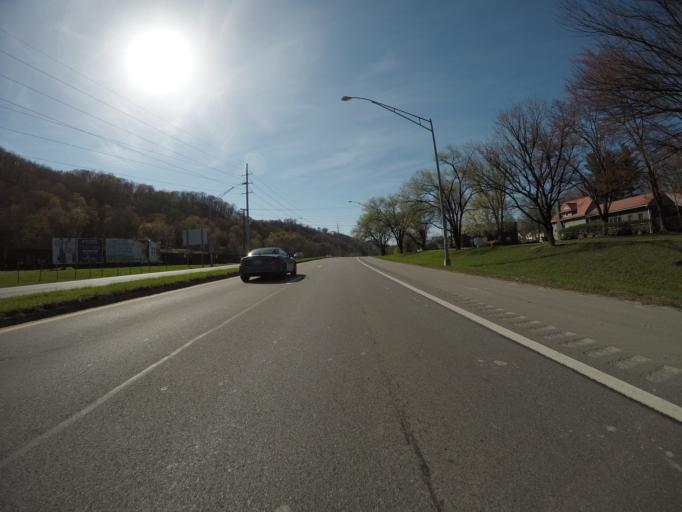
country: US
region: West Virginia
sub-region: Kanawha County
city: Charleston
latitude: 38.3290
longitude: -81.6061
